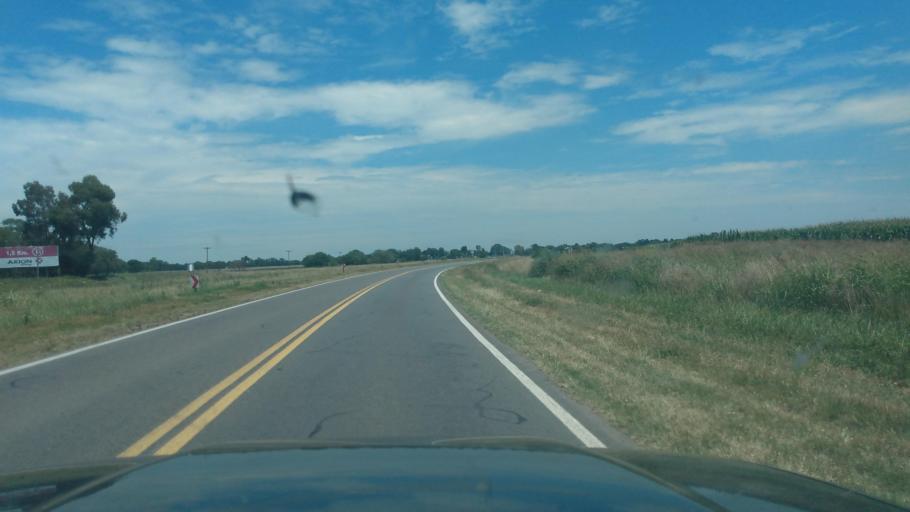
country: AR
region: Buenos Aires
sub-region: Partido de Pehuajo
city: Pehuajo
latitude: -35.8309
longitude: -61.8521
